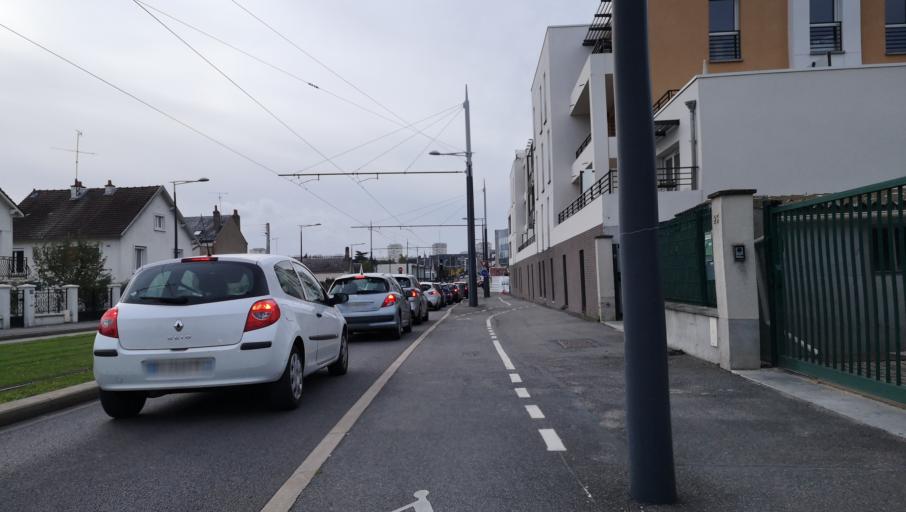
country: FR
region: Centre
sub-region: Departement du Loiret
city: Orleans
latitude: 47.9120
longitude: 1.9212
